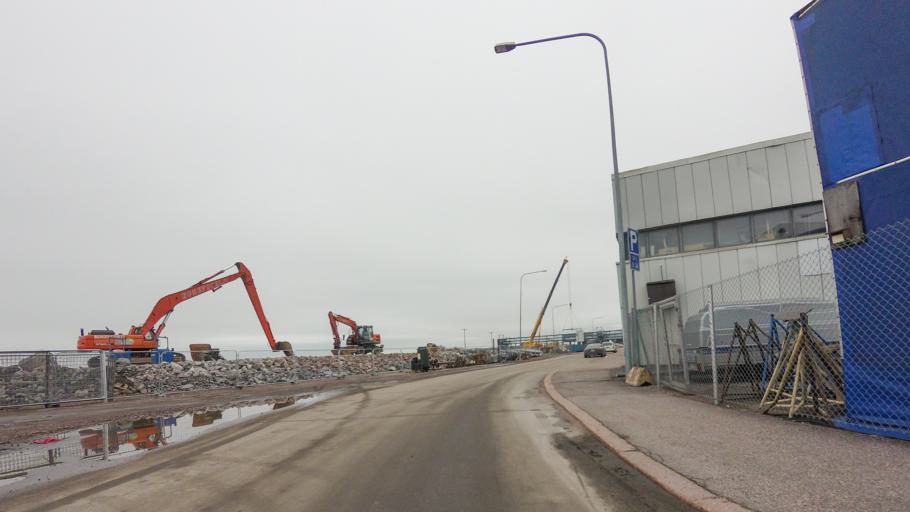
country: FI
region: Uusimaa
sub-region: Helsinki
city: Helsinki
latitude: 60.1478
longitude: 24.9223
